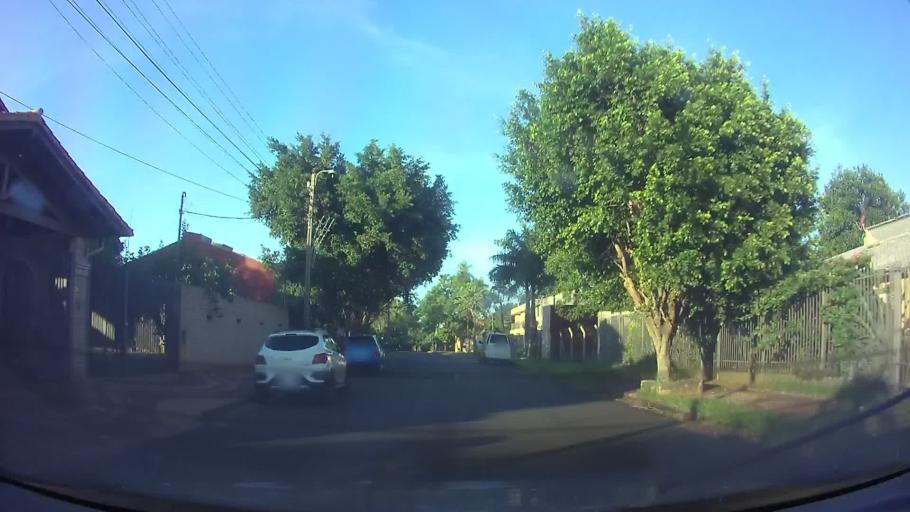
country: PY
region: Central
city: San Lorenzo
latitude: -25.2683
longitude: -57.5084
